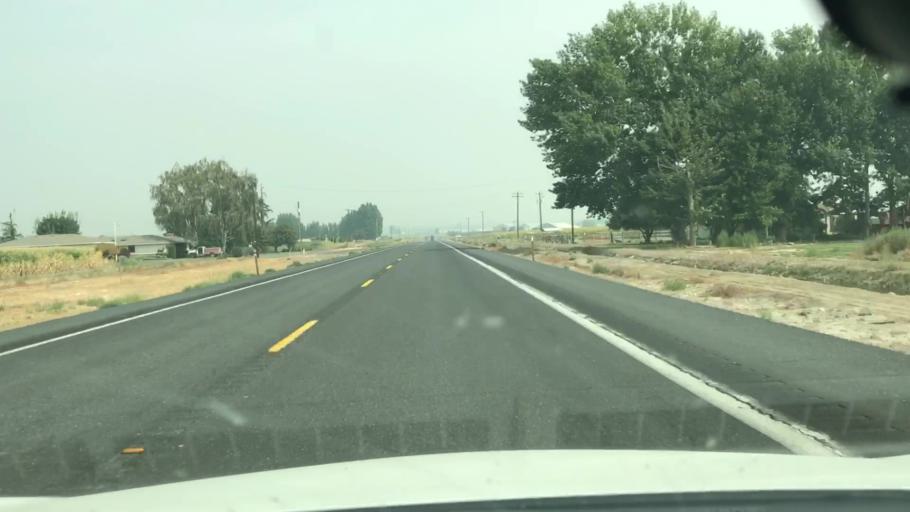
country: US
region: Washington
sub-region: Grant County
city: Quincy
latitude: 47.2369
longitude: -119.7428
